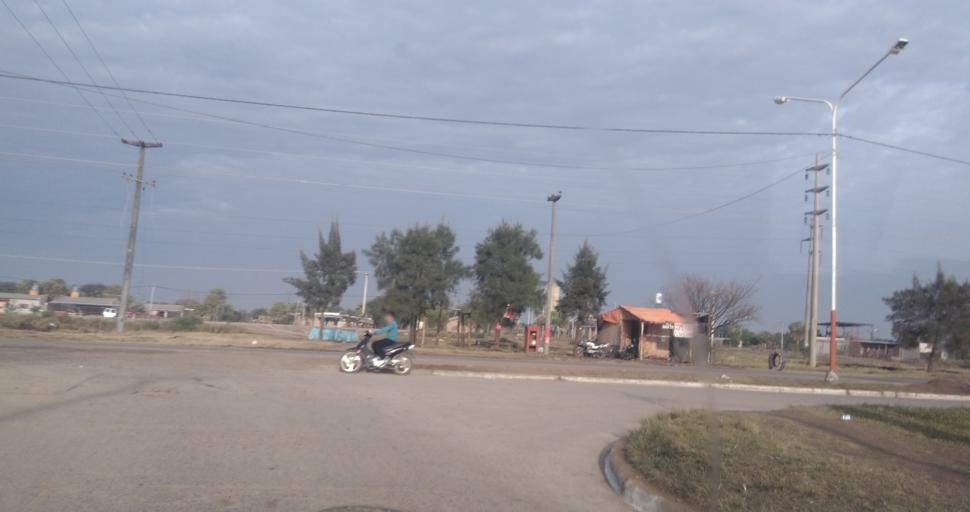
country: AR
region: Chaco
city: Resistencia
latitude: -27.4863
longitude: -58.9896
